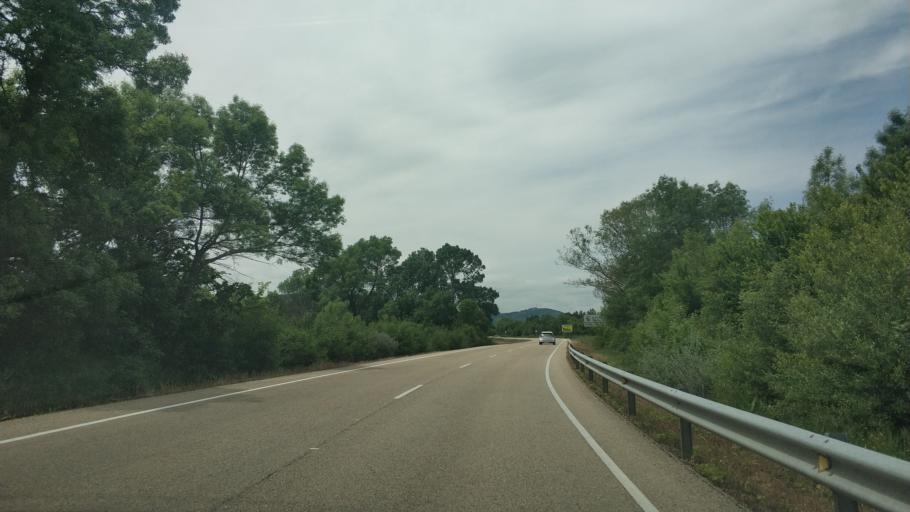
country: ES
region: Castille and Leon
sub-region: Provincia de Soria
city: Sotillo del Rincon
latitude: 41.9026
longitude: -2.6510
